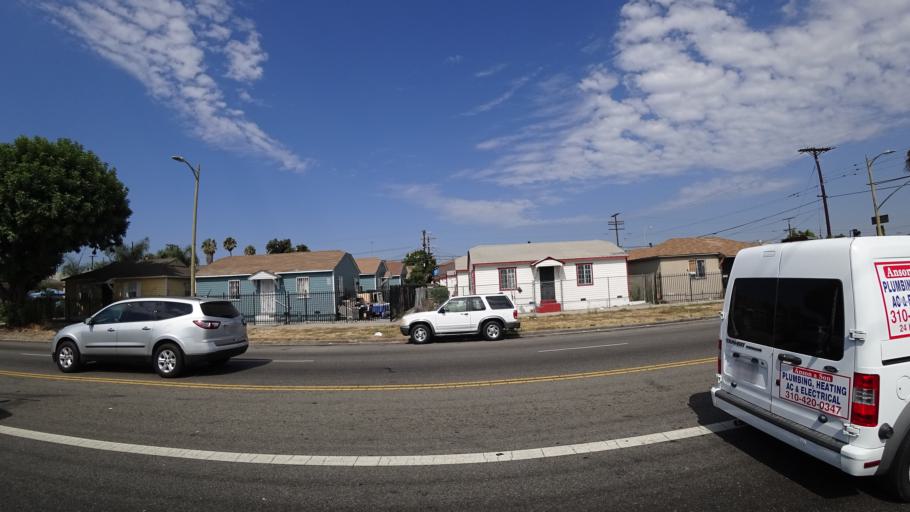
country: US
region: California
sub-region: Los Angeles County
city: Westmont
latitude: 33.9524
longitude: -118.3090
